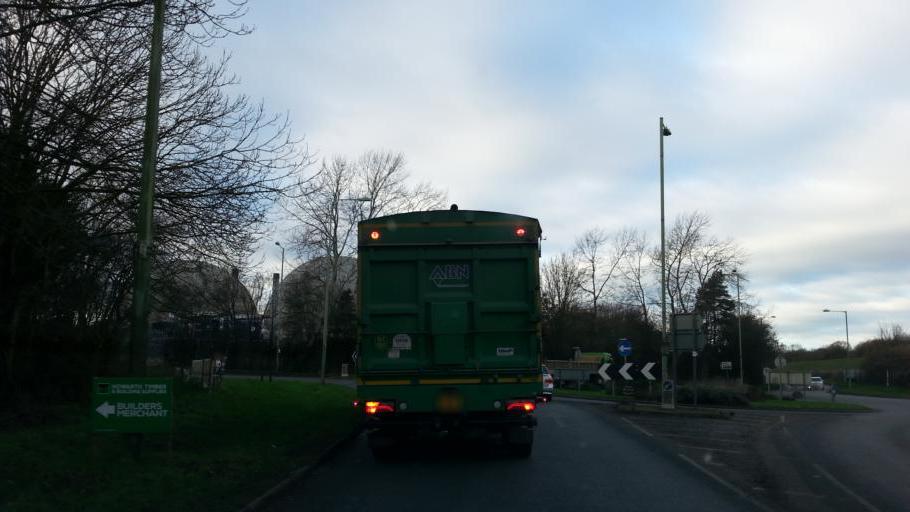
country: GB
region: England
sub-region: Suffolk
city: Bury St Edmunds
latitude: 52.2574
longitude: 0.7311
